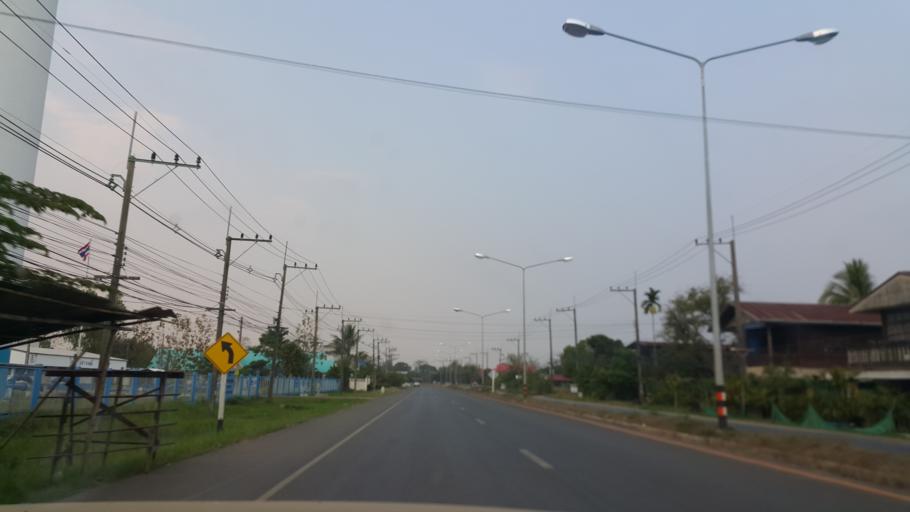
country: TH
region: Nakhon Phanom
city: That Phanom
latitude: 16.9810
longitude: 104.7278
